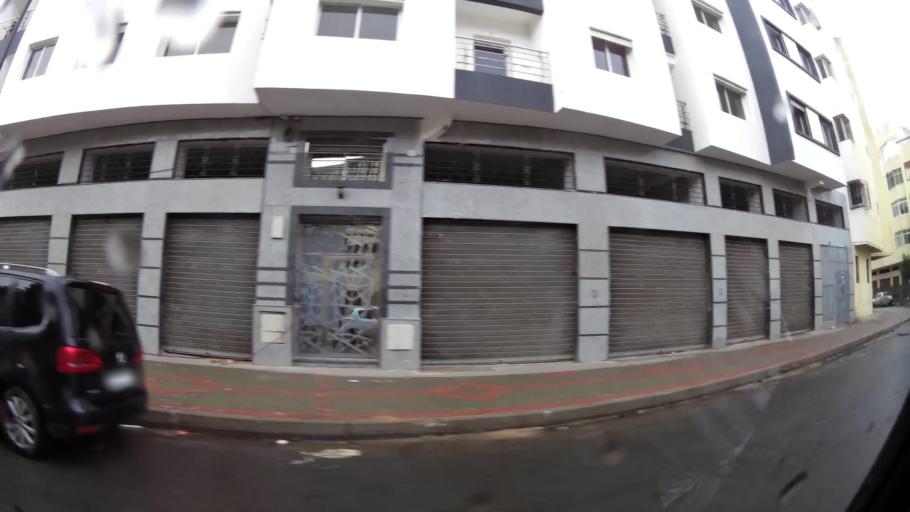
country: MA
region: Grand Casablanca
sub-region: Casablanca
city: Casablanca
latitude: 33.5498
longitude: -7.5845
